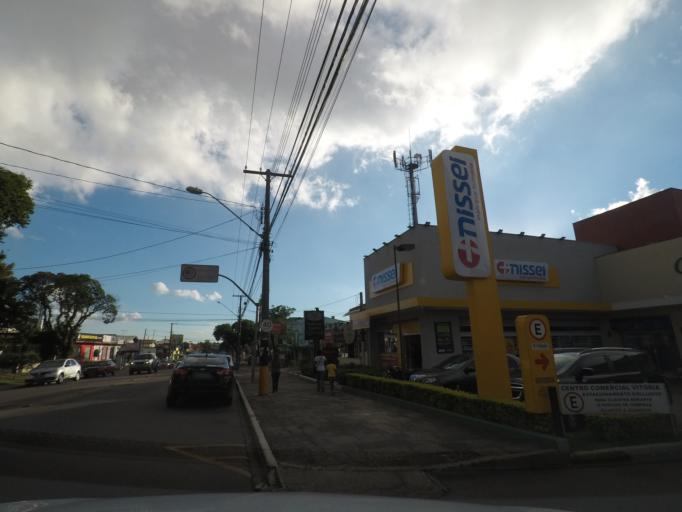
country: BR
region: Parana
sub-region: Sao Jose Dos Pinhais
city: Sao Jose dos Pinhais
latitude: -25.5010
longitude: -49.2535
